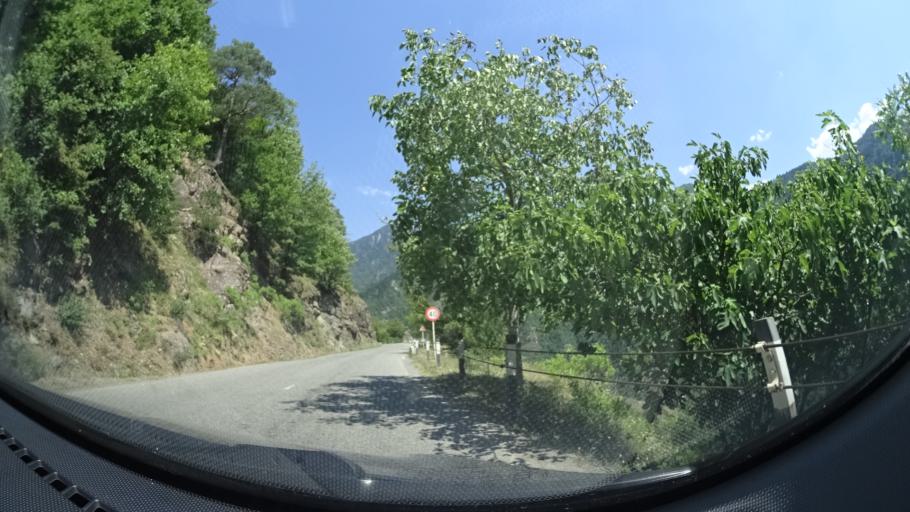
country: GE
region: Ajaria
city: Khulo
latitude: 41.6285
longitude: 42.2940
